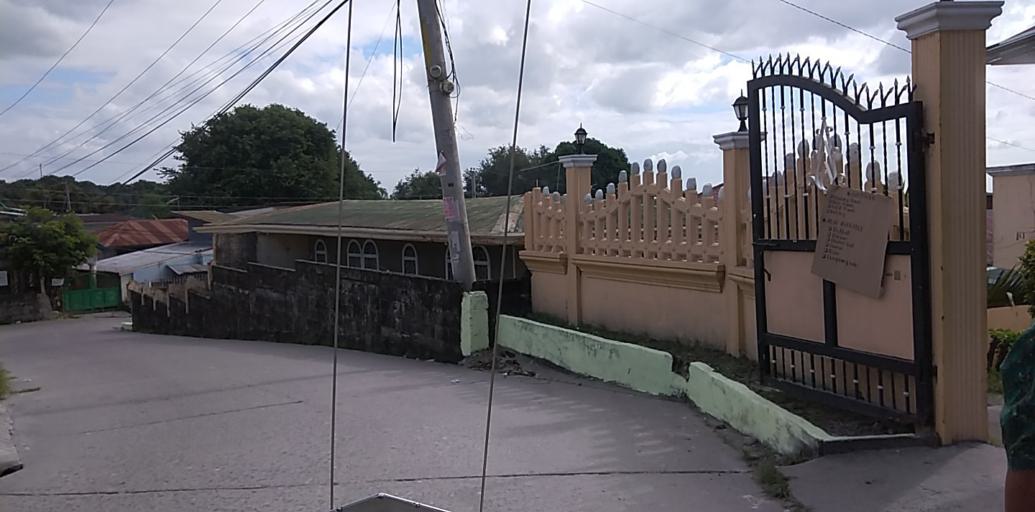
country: PH
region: Central Luzon
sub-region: Province of Pampanga
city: Porac
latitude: 15.0765
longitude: 120.5342
